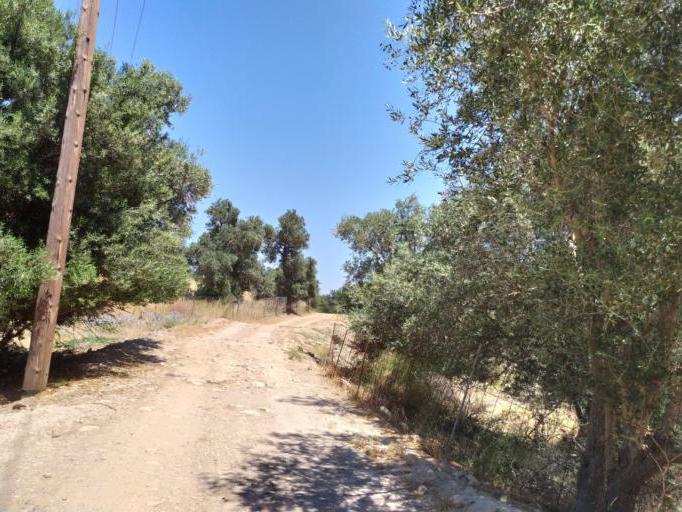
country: GR
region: Crete
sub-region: Nomos Irakleiou
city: Agioi Deka
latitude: 35.0592
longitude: 24.9486
